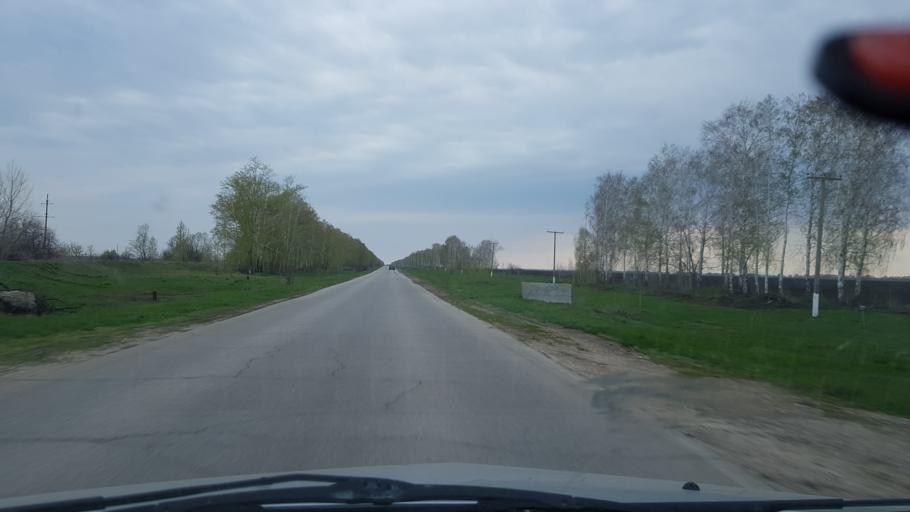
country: RU
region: Samara
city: Tol'yatti
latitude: 53.6584
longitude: 49.2407
